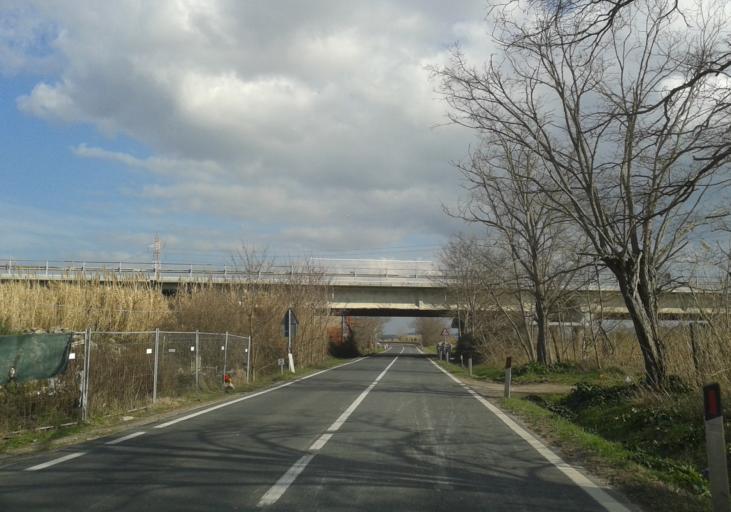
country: IT
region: Tuscany
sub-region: Provincia di Livorno
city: Guasticce
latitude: 43.6028
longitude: 10.3563
